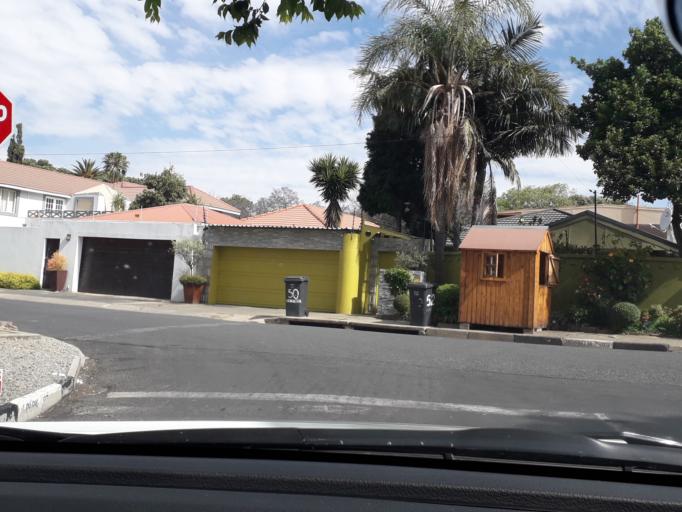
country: ZA
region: Gauteng
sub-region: City of Johannesburg Metropolitan Municipality
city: Johannesburg
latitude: -26.1553
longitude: 28.0702
